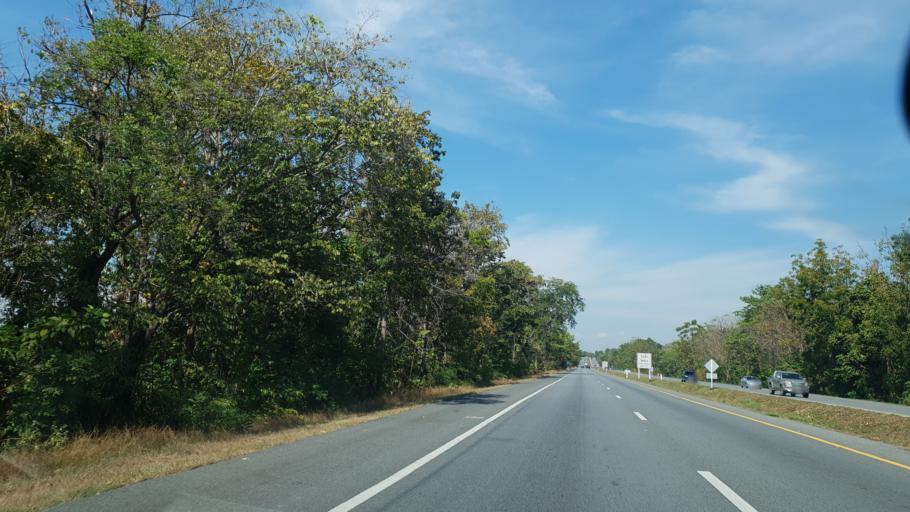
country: TH
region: Uttaradit
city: Thong Saen Khan
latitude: 17.4091
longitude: 100.2293
